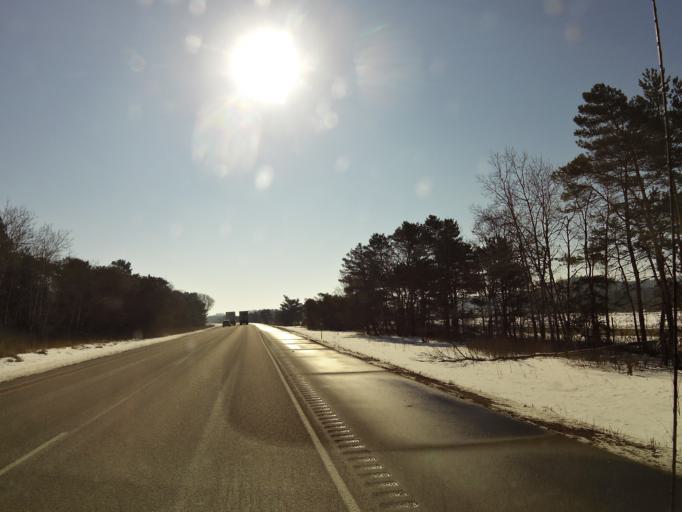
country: US
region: Wisconsin
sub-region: Trempealeau County
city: Osseo
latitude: 44.5266
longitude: -91.1497
